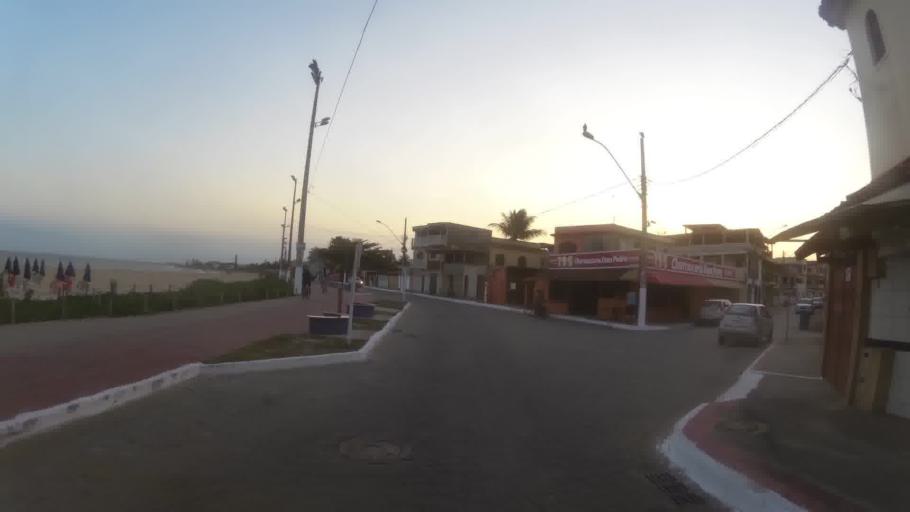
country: BR
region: Espirito Santo
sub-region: Piuma
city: Piuma
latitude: -20.9055
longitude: -40.7797
